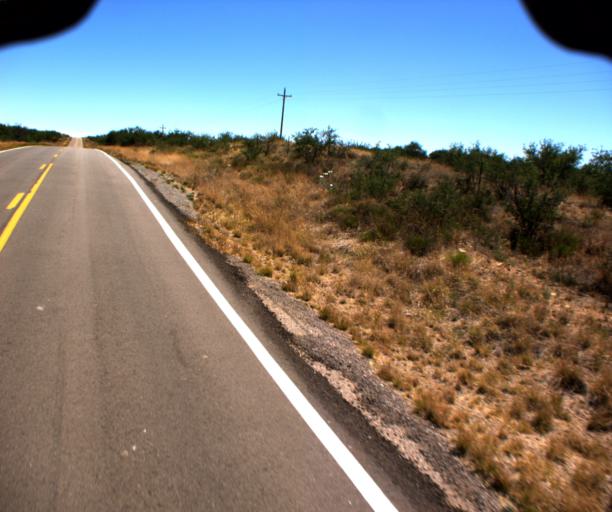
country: US
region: Arizona
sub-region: Santa Cruz County
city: Tubac
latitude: 31.5357
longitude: -111.5409
